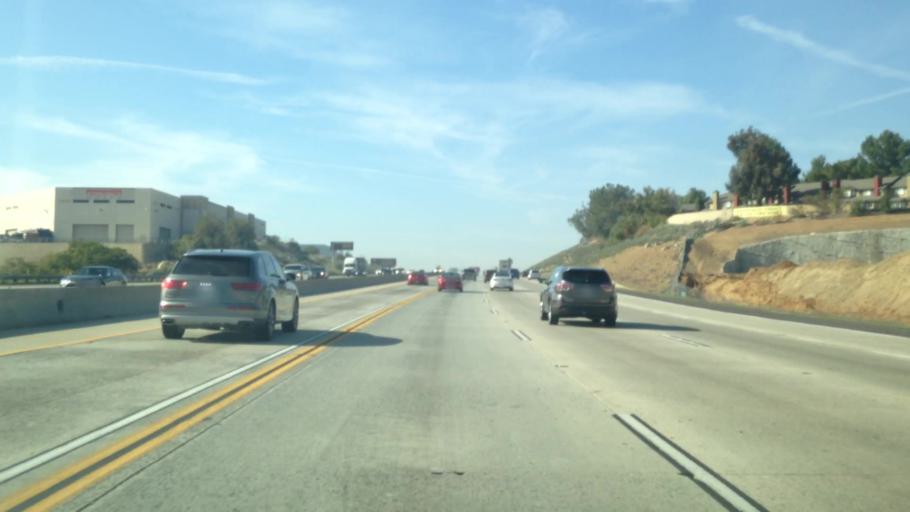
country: US
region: California
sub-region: Riverside County
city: Home Gardens
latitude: 33.8843
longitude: -117.5256
